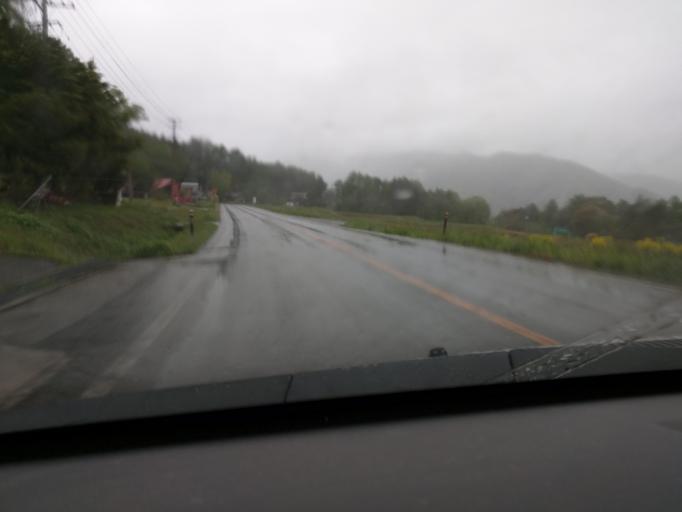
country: JP
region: Fukushima
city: Inawashiro
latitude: 37.5892
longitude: 140.1255
